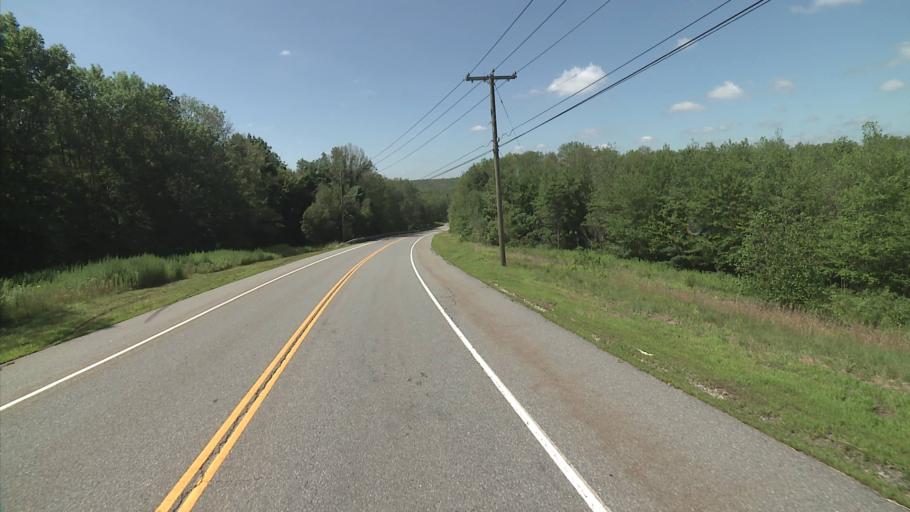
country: US
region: Connecticut
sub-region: Windham County
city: Moosup
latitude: 41.6850
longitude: -71.8585
